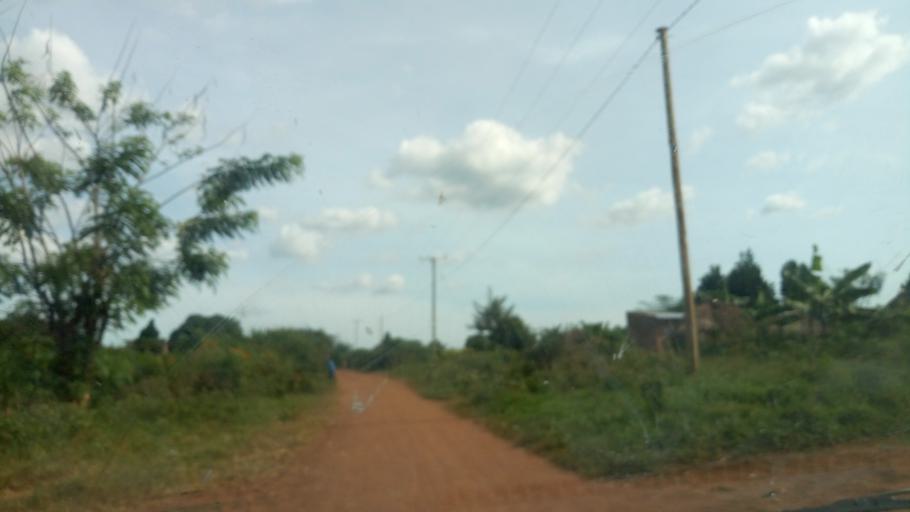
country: UG
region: Western Region
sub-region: Kiryandongo District
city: Kiryandongo
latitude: 1.8113
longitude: 31.9406
